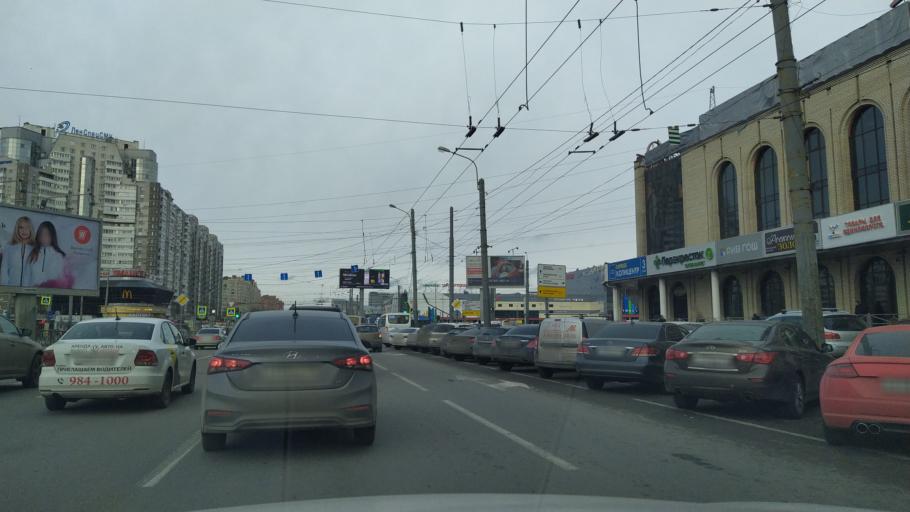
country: RU
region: Leningrad
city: Chernaya Rechka
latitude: 60.0019
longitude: 30.2986
